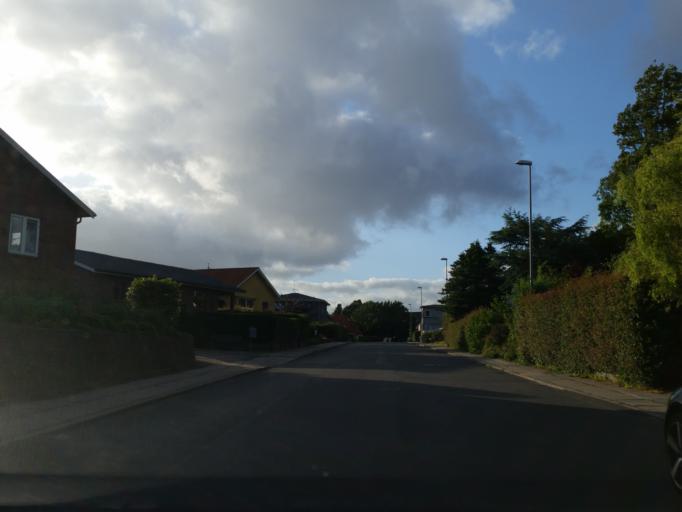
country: DK
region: South Denmark
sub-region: Vejle Kommune
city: Brejning
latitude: 55.6639
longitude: 9.6730
